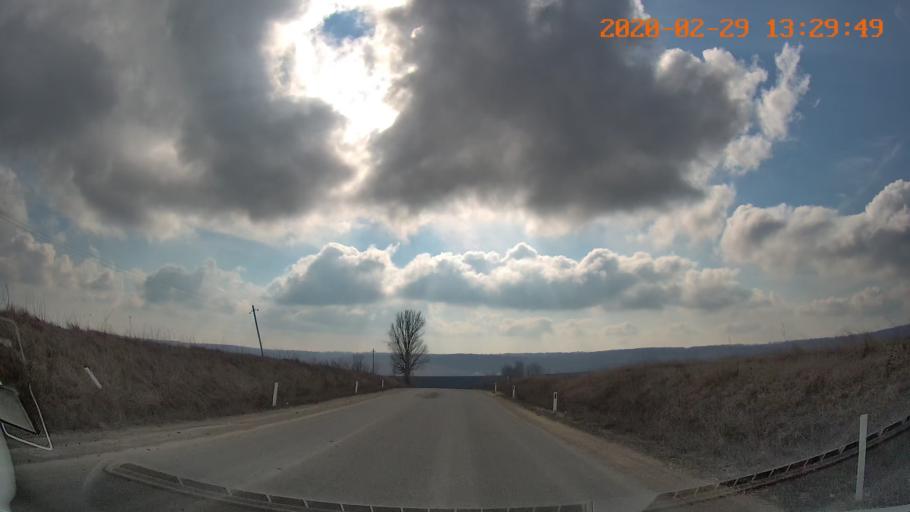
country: MD
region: Telenesti
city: Camenca
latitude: 47.8931
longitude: 28.6335
